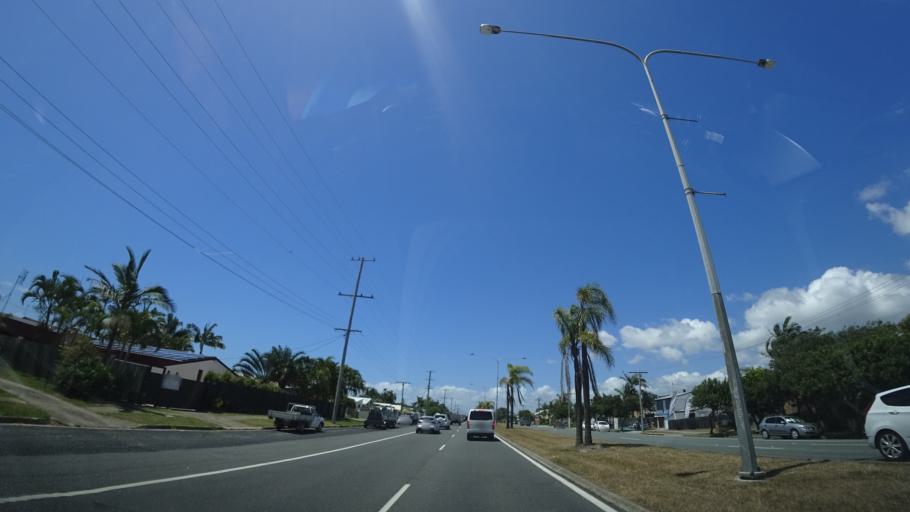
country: AU
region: Queensland
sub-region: Sunshine Coast
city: Mooloolaba
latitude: -26.7109
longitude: 153.1301
